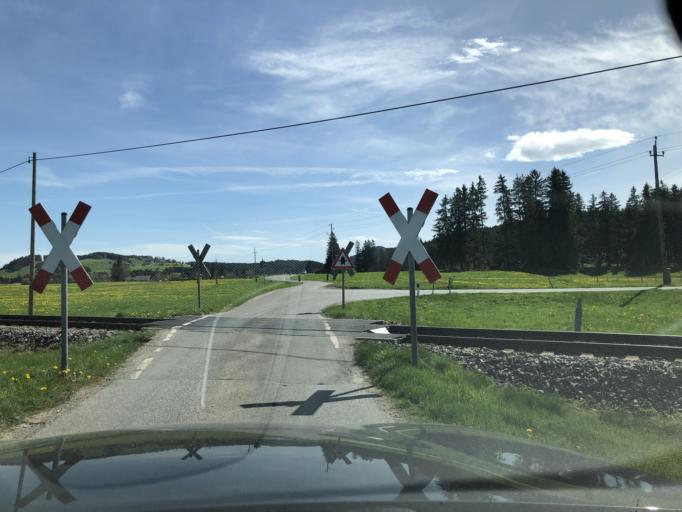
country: DE
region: Bavaria
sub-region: Swabia
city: Seeg
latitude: 47.6399
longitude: 10.6062
